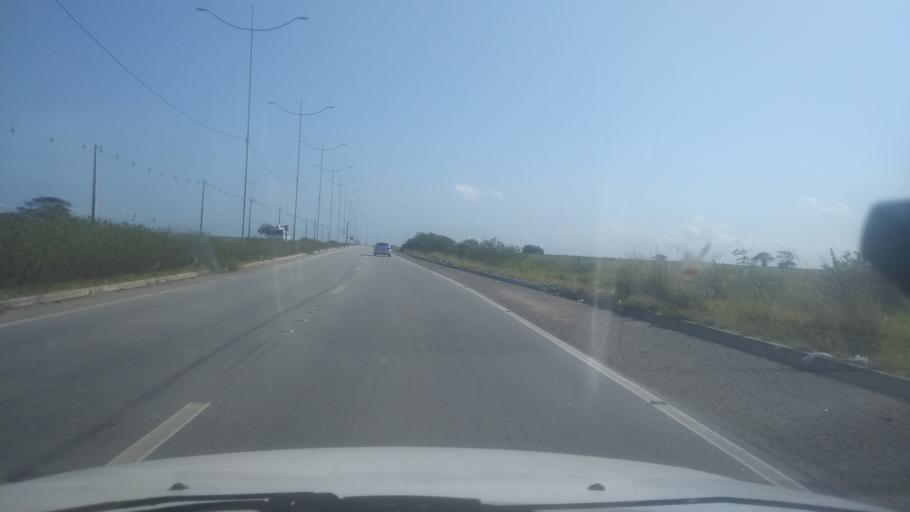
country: BR
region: Rio Grande do Norte
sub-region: Macaiba
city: Macaiba
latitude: -5.8296
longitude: -35.3701
